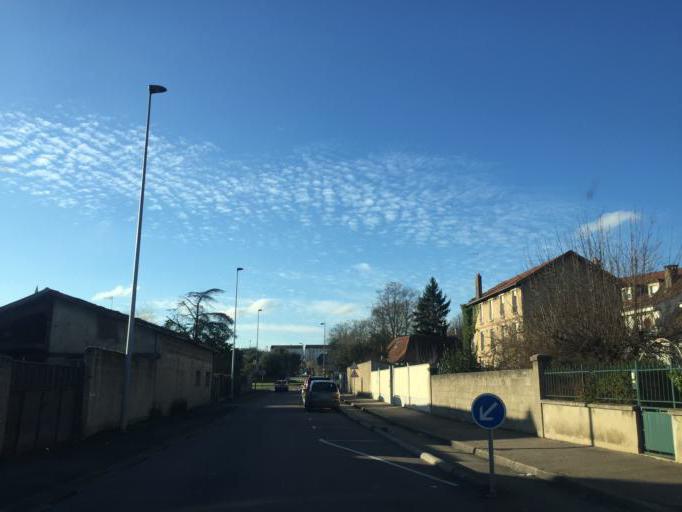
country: FR
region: Bourgogne
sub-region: Departement de l'Yonne
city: Auxerre
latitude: 47.8013
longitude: 3.5791
